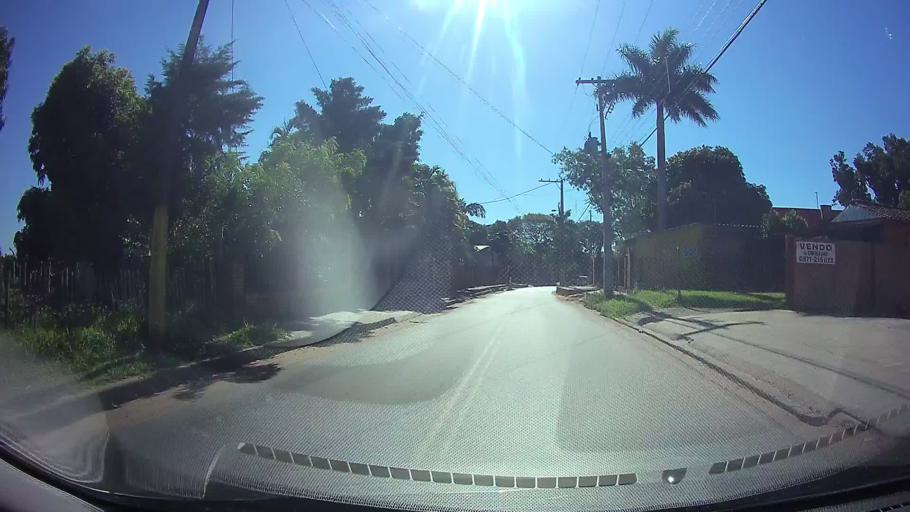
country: PY
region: Central
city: Fernando de la Mora
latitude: -25.2975
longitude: -57.5316
